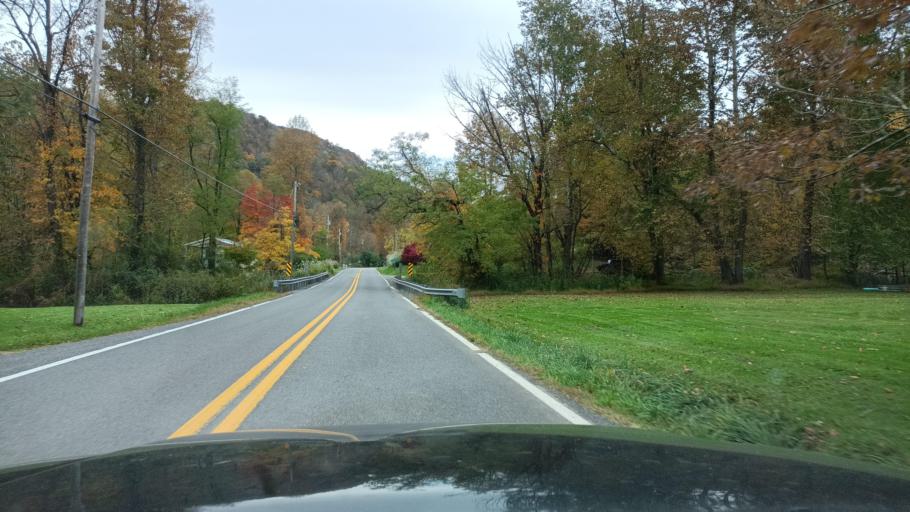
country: US
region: West Virginia
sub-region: Preston County
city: Kingwood
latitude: 39.3133
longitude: -79.6489
